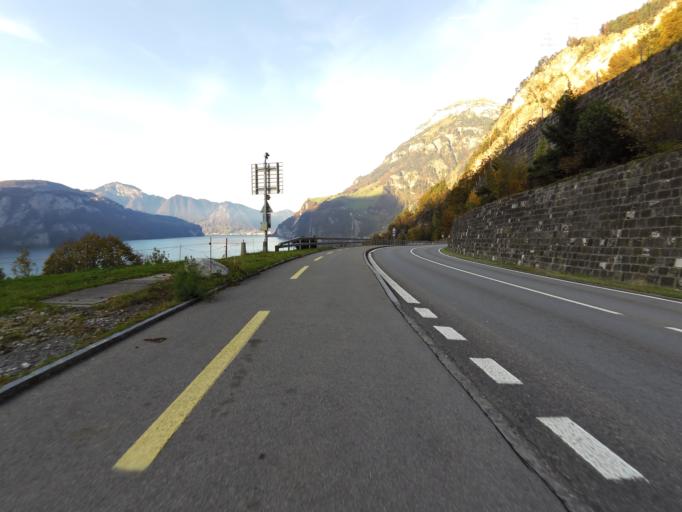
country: CH
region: Uri
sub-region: Uri
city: Flueelen
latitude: 46.9352
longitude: 8.6144
